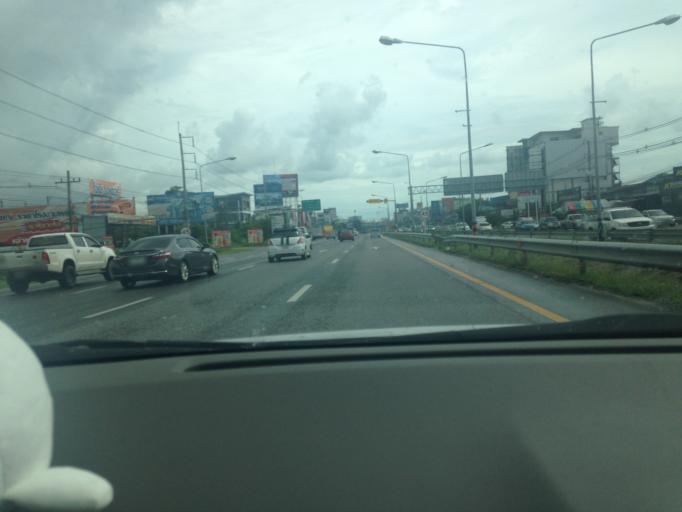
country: TH
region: Chon Buri
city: Chon Buri
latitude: 13.2929
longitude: 100.9436
